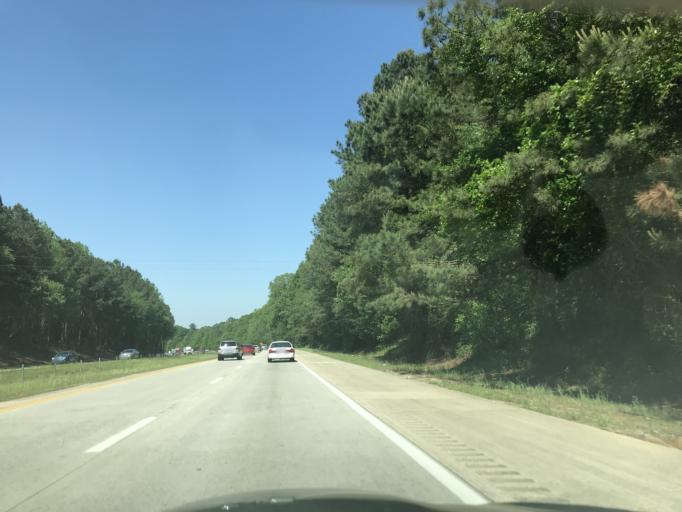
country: US
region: North Carolina
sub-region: Johnston County
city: Clayton
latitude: 35.5564
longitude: -78.5771
